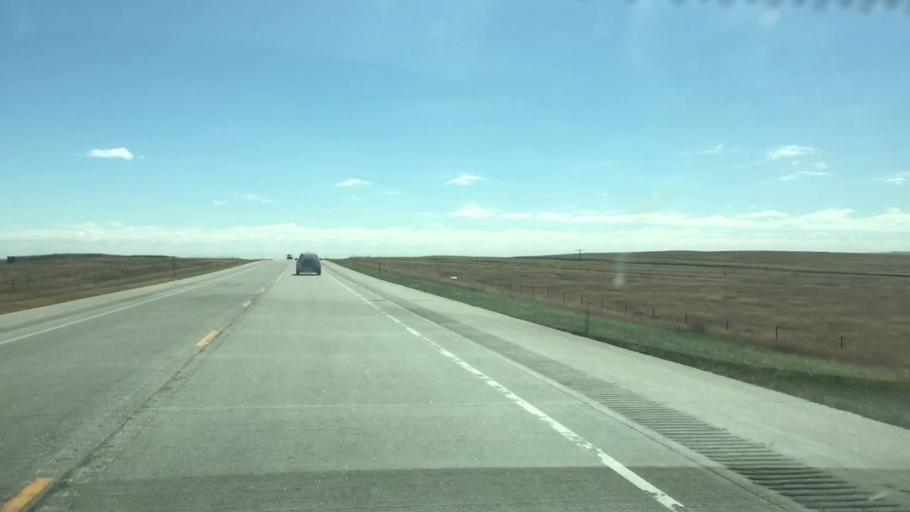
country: US
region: Colorado
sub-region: Lincoln County
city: Hugo
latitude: 39.1774
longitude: -103.5421
